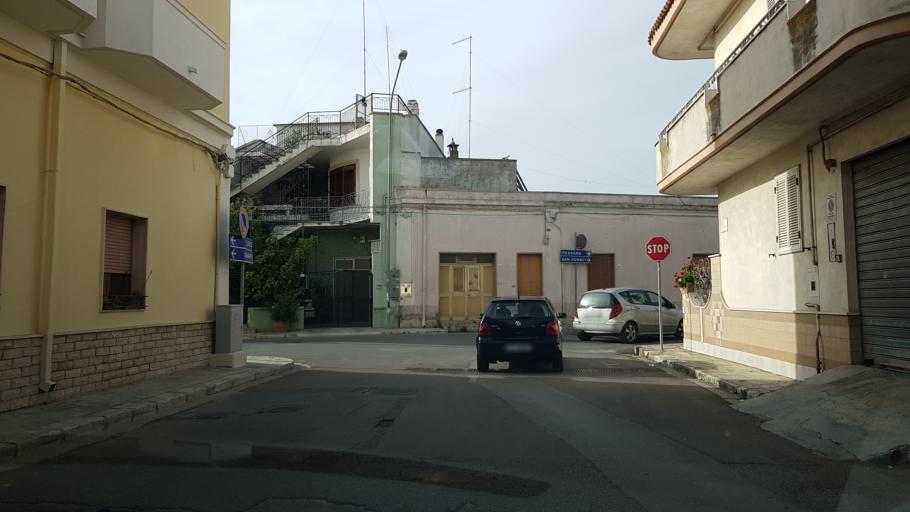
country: IT
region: Apulia
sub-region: Provincia di Brindisi
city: San Pancrazio Salentino
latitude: 40.4194
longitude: 17.8443
